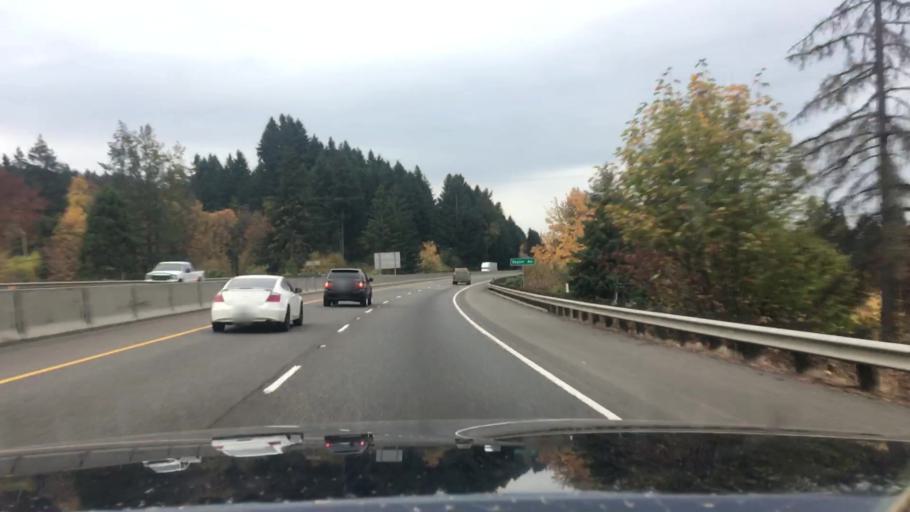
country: US
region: Oregon
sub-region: Lane County
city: Cottage Grove
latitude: 43.7877
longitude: -123.0535
